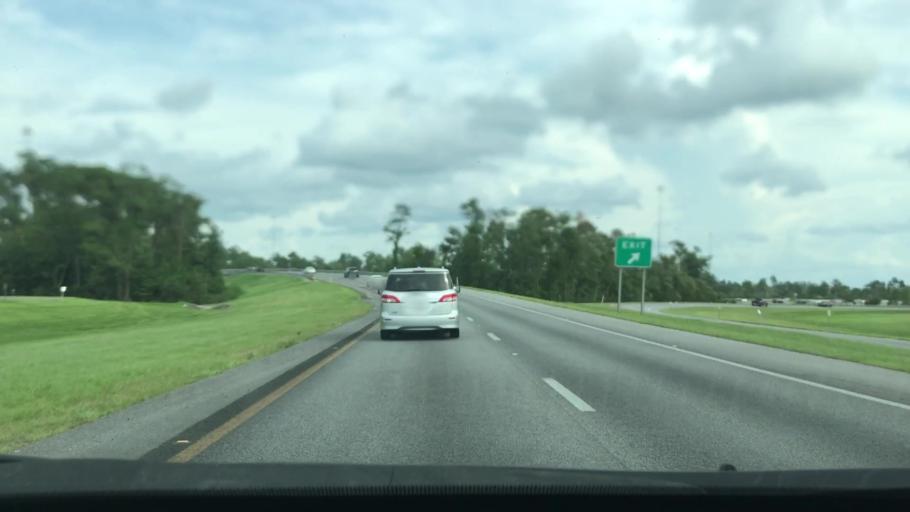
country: US
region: Florida
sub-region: Osceola County
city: Celebration
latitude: 28.3588
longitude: -81.5251
